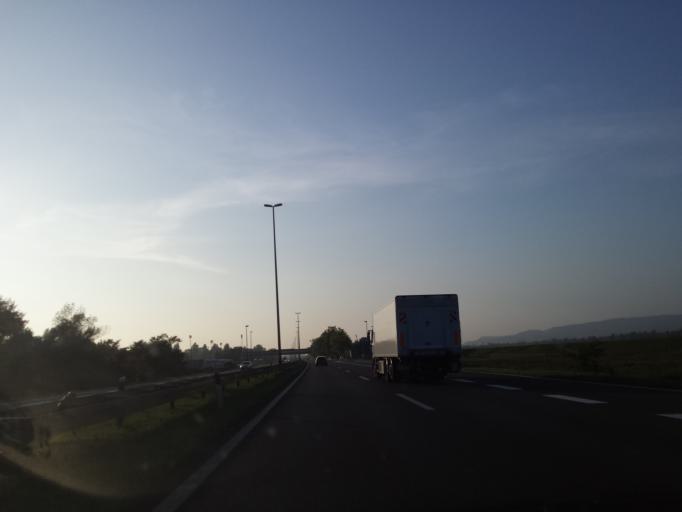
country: HR
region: Grad Zagreb
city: Lucko
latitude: 45.7719
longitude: 15.8844
